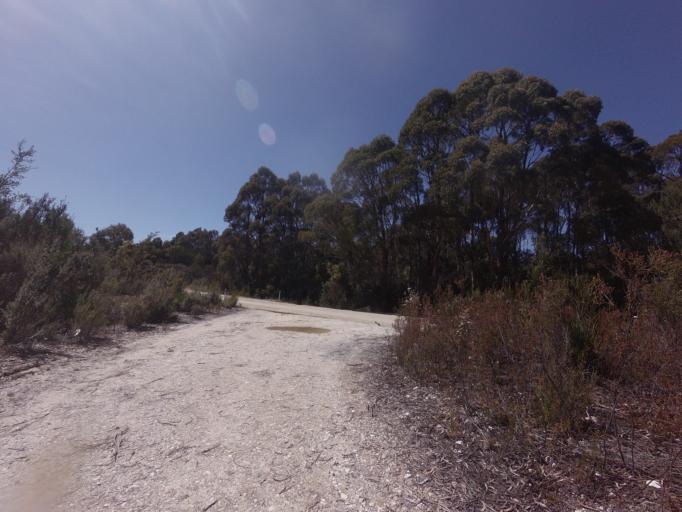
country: AU
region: Tasmania
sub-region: Huon Valley
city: Geeveston
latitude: -43.0289
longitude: 146.3506
